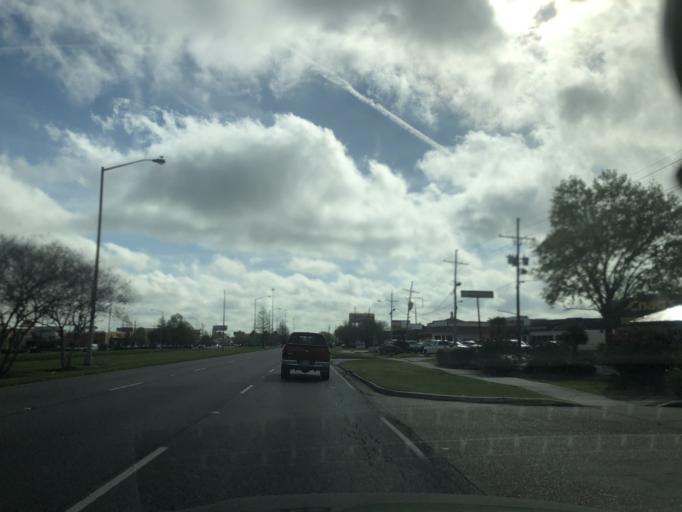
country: US
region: Louisiana
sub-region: Jefferson Parish
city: Metairie Terrace
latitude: 30.0052
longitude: -90.1902
